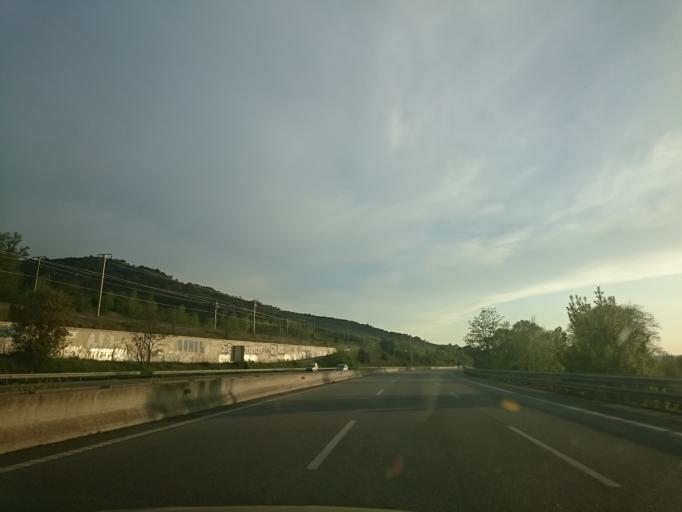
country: ES
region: Catalonia
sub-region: Provincia de Barcelona
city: Llinars del Valles
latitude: 41.6343
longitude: 2.4014
